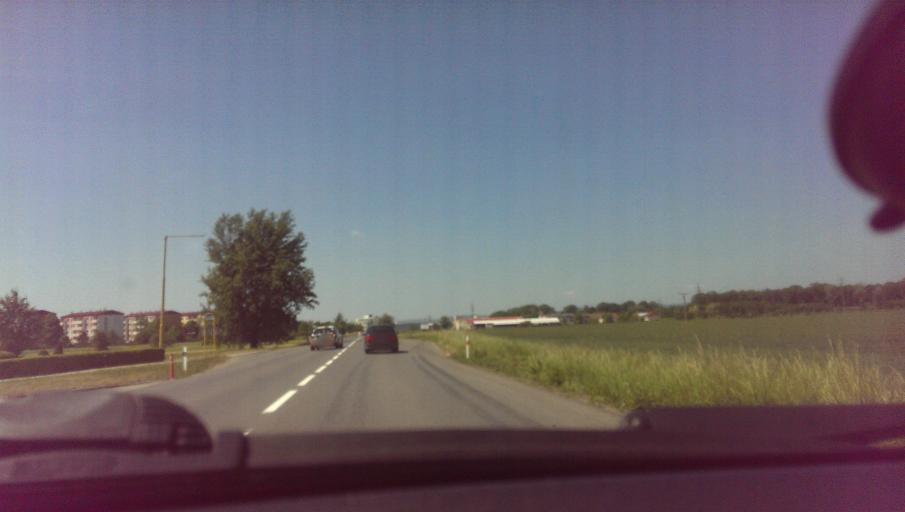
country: CZ
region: Zlin
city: Knezpole
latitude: 49.0905
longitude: 17.5072
